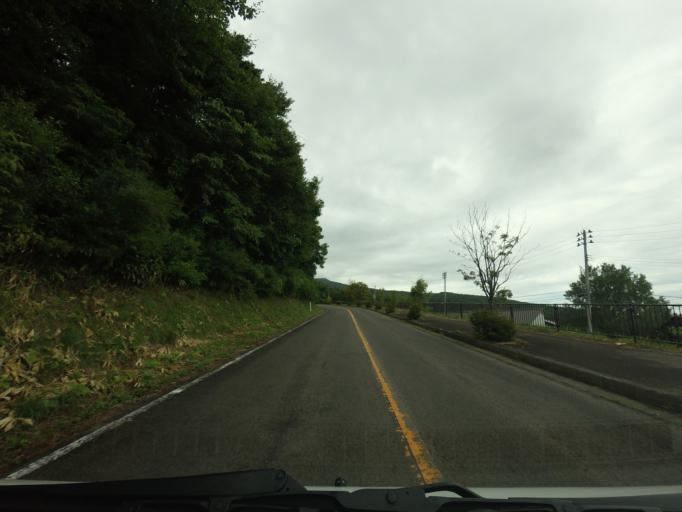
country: JP
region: Fukushima
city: Motomiya
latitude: 37.5812
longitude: 140.3355
